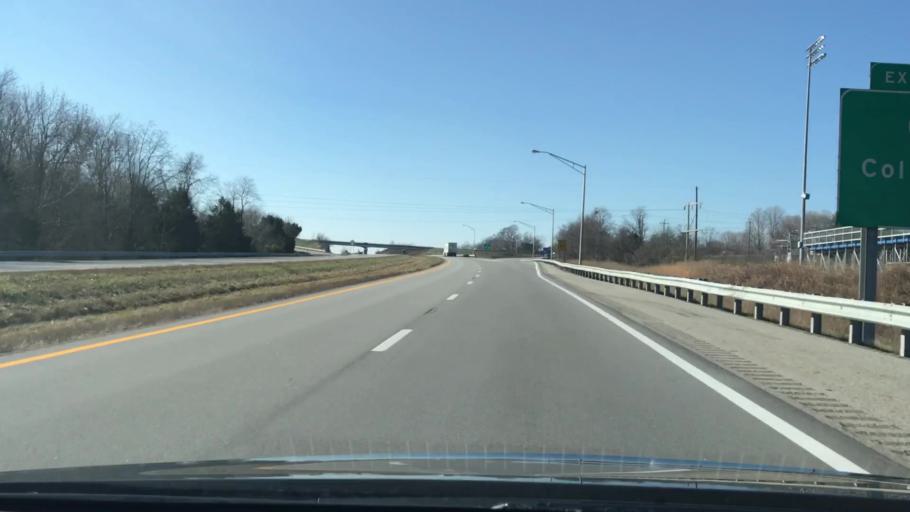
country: US
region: Kentucky
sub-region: Adair County
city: Columbia
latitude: 37.0892
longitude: -85.2973
